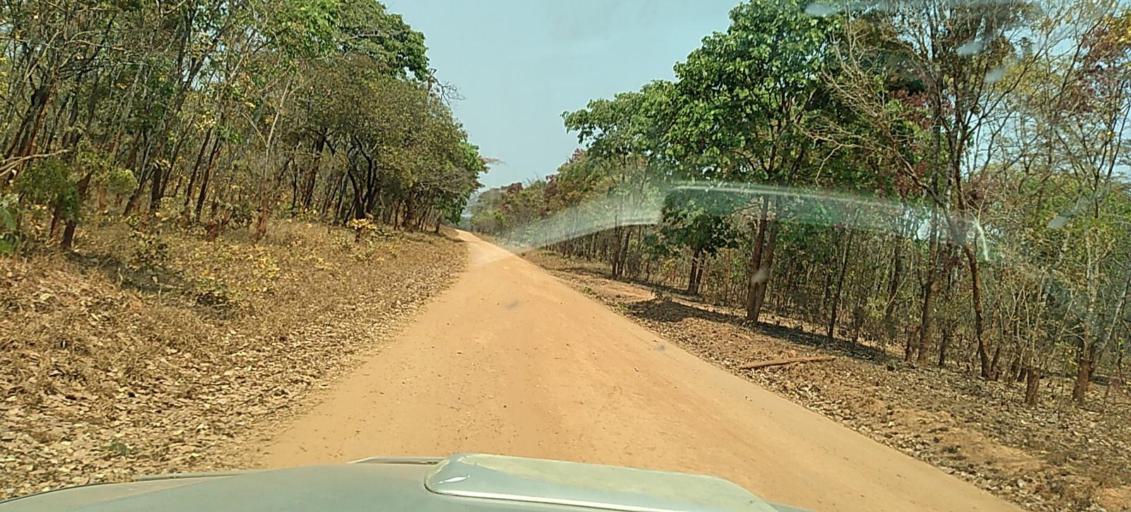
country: ZM
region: North-Western
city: Kasempa
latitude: -13.6701
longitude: 26.2968
